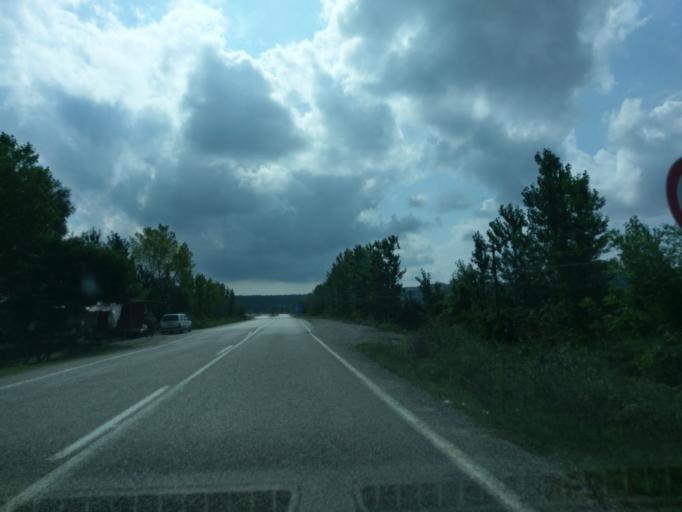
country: TR
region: Sinop
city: Sinop
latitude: 42.0143
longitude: 35.0553
